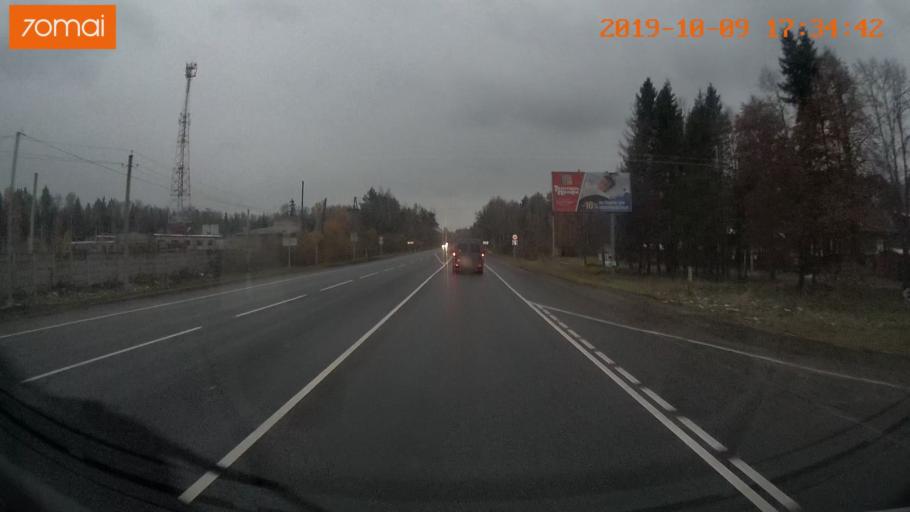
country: RU
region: Ivanovo
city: Bogorodskoye
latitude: 57.1042
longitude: 41.0094
